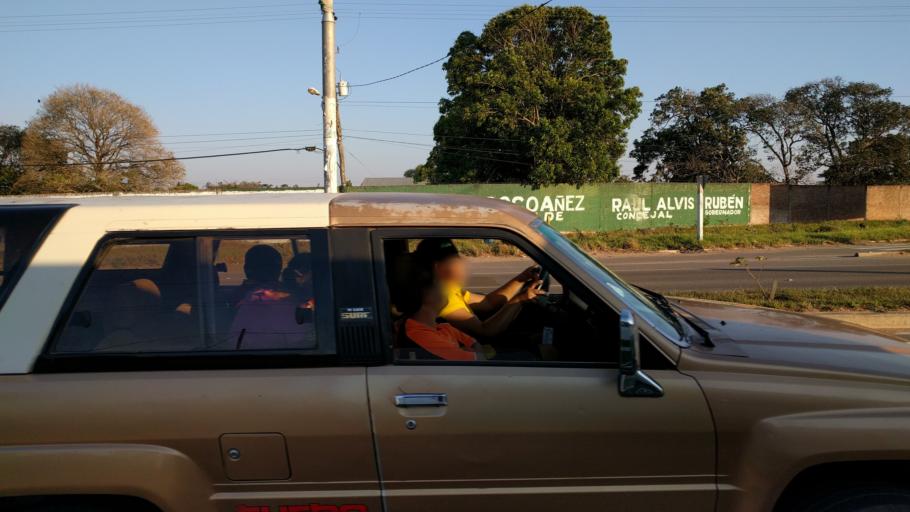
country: BO
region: Santa Cruz
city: Cotoca
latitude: -17.7586
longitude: -63.0111
